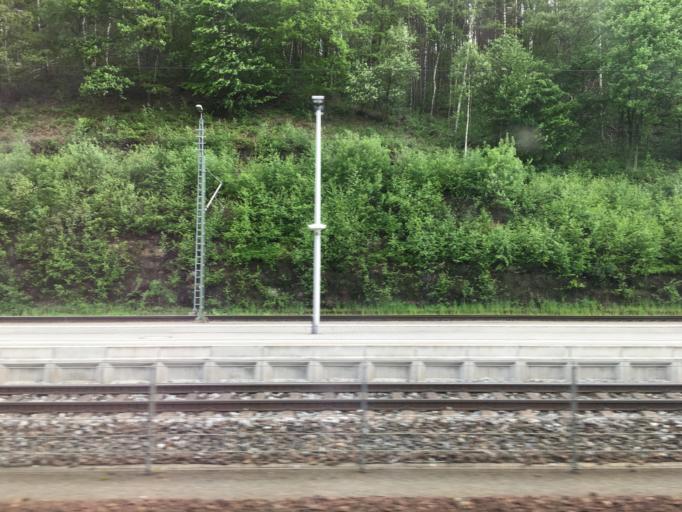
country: DE
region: Saxony
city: Rathmannsdorf
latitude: 50.9192
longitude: 14.1379
